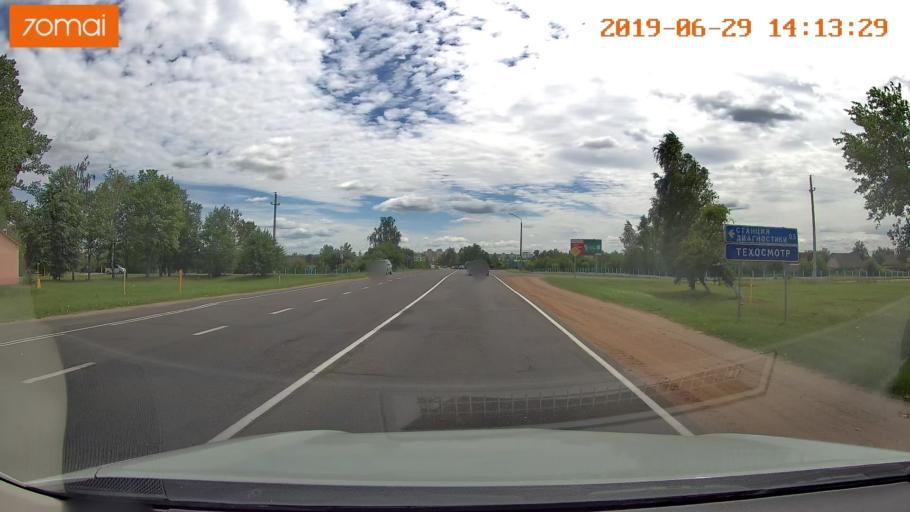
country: BY
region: Minsk
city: Salihorsk
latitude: 52.8028
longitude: 27.5108
